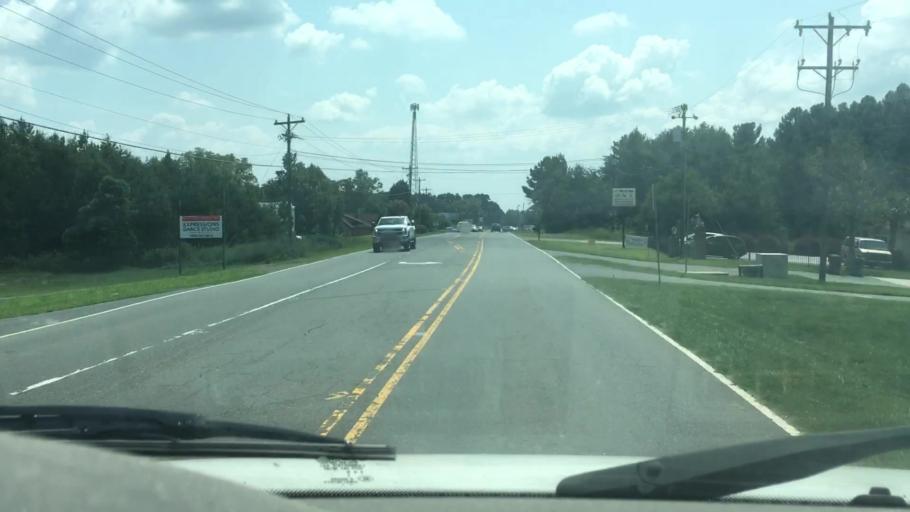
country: US
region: North Carolina
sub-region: Lincoln County
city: Westport
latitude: 35.4865
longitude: -80.9952
